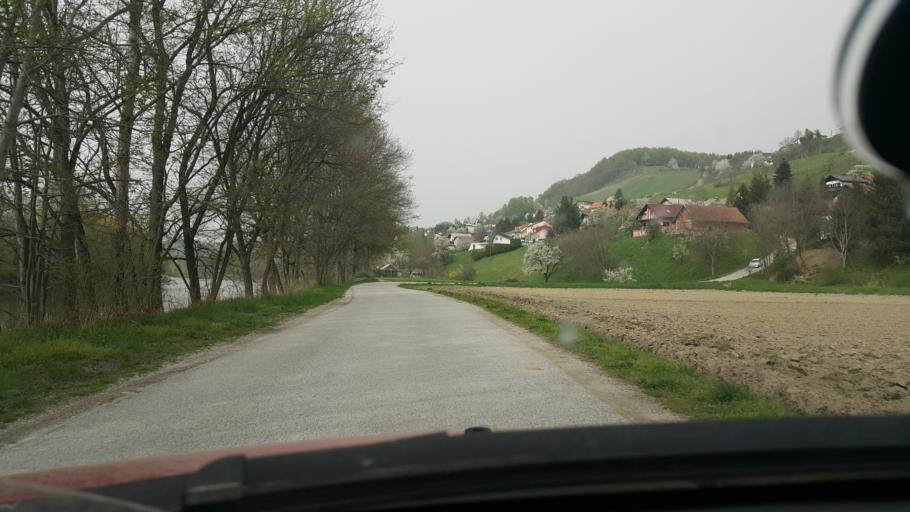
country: SI
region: Duplek
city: Zgornji Duplek
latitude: 46.5327
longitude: 15.7190
